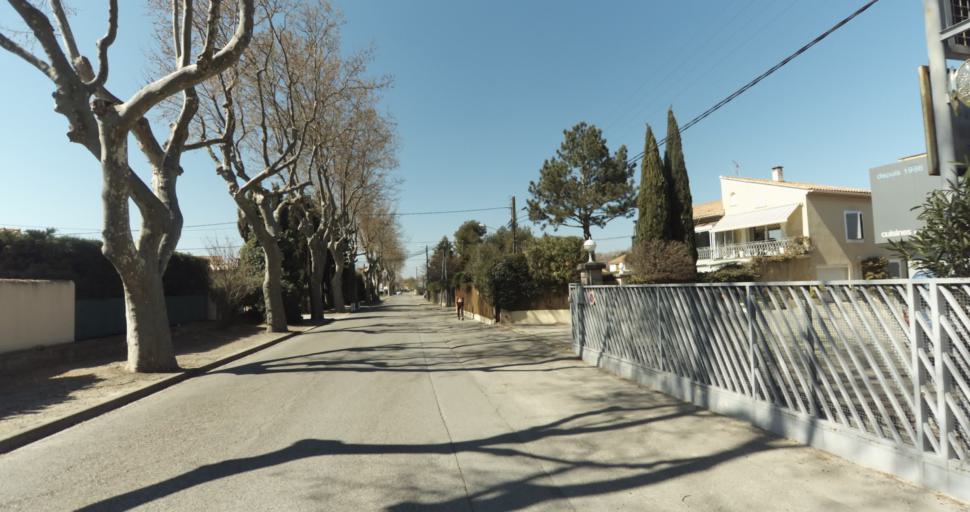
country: FR
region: Provence-Alpes-Cote d'Azur
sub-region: Departement des Bouches-du-Rhone
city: Pelissanne
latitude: 43.6288
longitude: 5.1590
